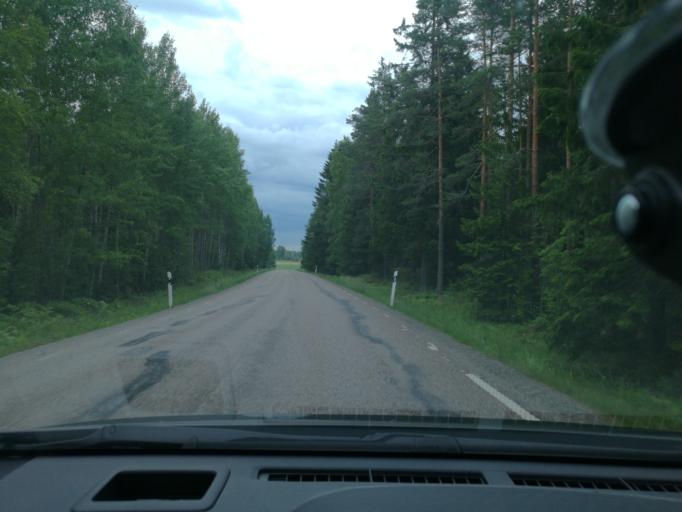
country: SE
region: Vaestmanland
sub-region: Sala Kommun
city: Sala
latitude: 59.9114
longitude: 16.4201
